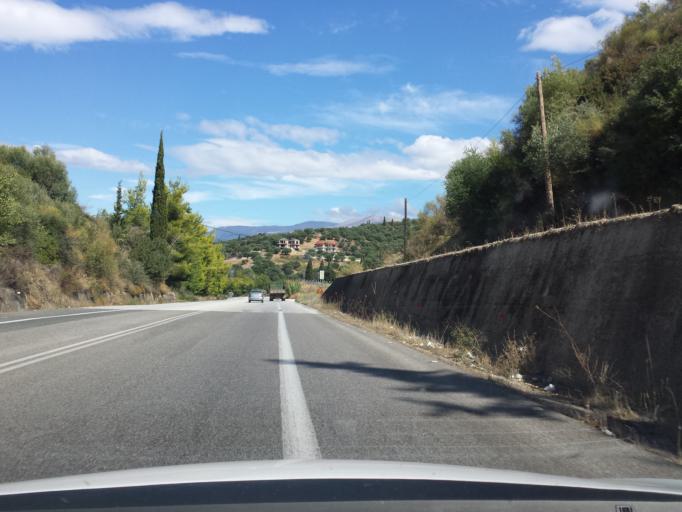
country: GR
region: West Greece
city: Vrachnaiika
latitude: 38.1605
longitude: 21.6735
